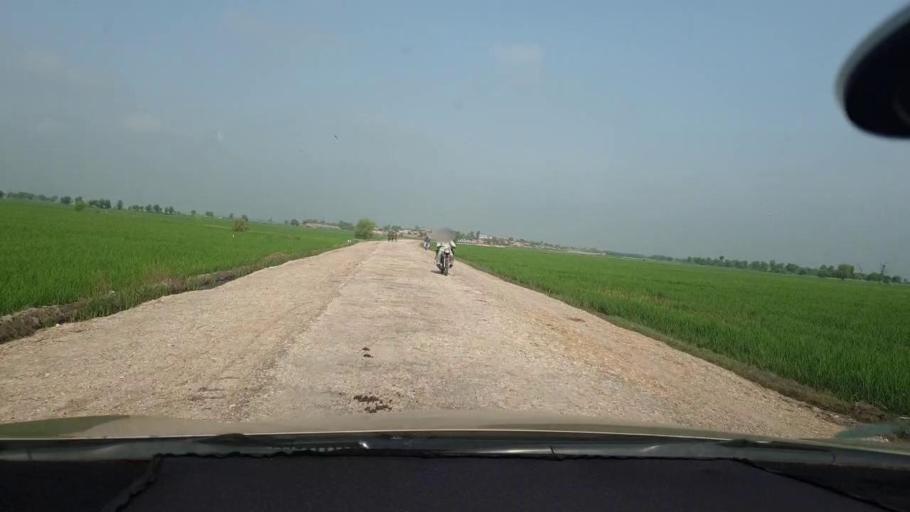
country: PK
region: Sindh
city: Kambar
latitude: 27.5390
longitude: 68.0537
